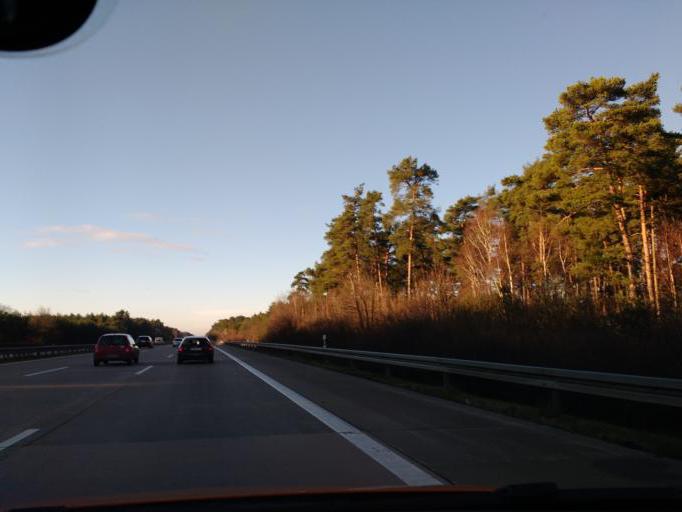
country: DE
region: Brandenburg
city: Wenzlow
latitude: 52.2753
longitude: 12.4158
